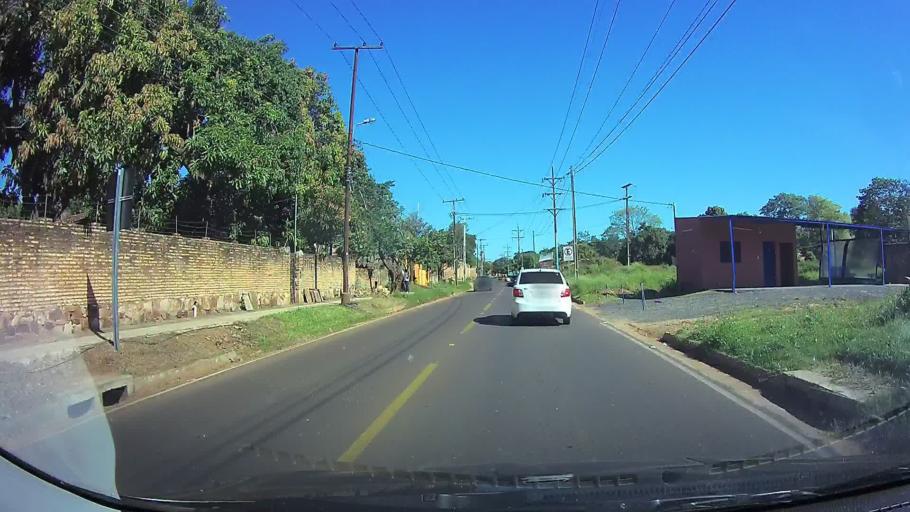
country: PY
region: Central
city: Fernando de la Mora
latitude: -25.3143
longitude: -57.5231
